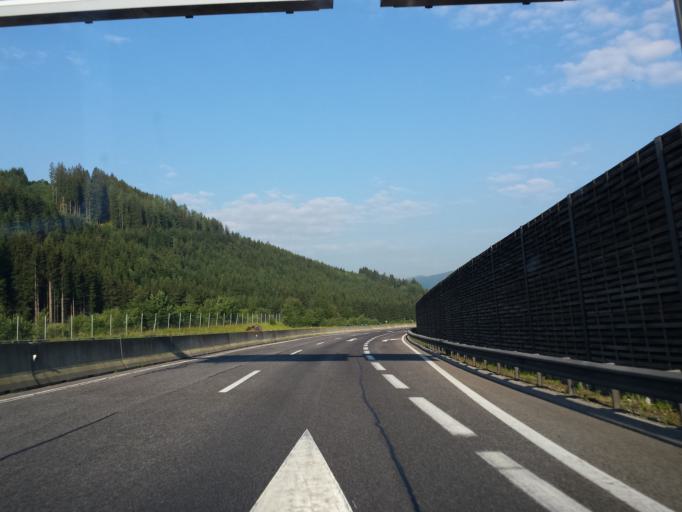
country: AT
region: Styria
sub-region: Politischer Bezirk Bruck-Muerzzuschlag
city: Spital am Semmering
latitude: 47.6009
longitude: 15.7272
